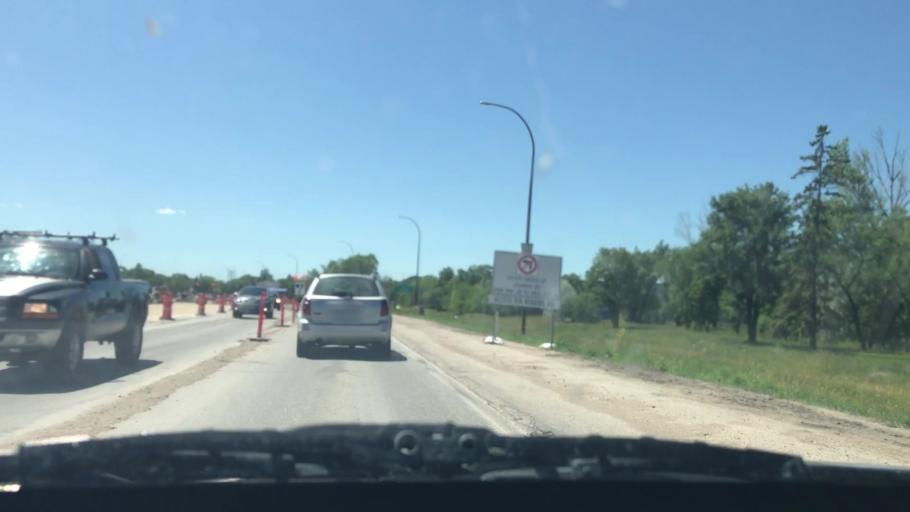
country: CA
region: Manitoba
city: Winnipeg
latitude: 49.8575
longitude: -97.0995
